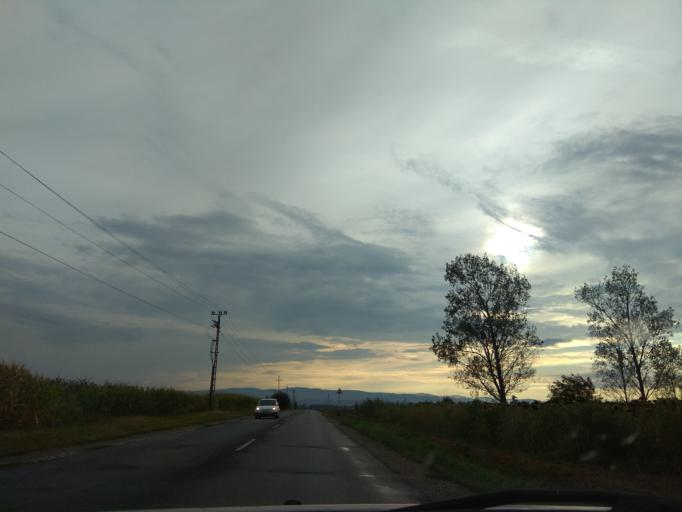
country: HU
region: Borsod-Abauj-Zemplen
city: Felsozsolca
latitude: 48.1153
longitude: 20.8850
